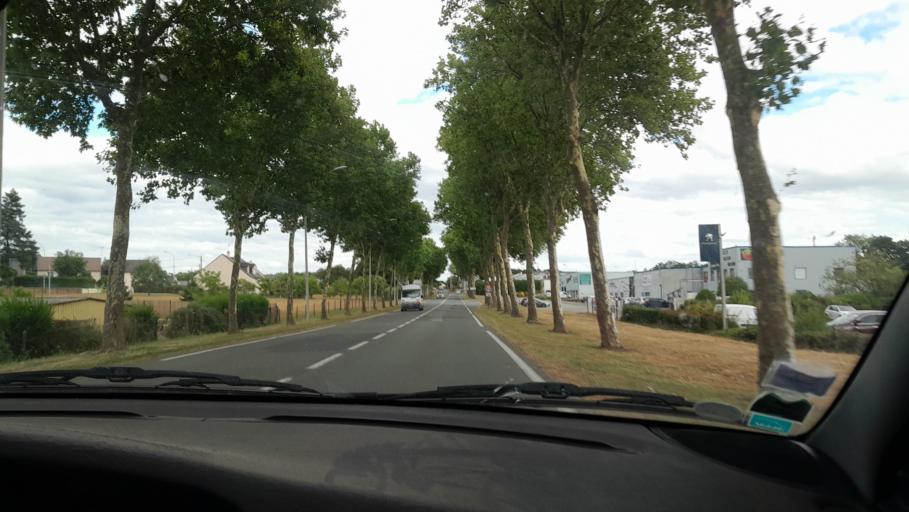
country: FR
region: Pays de la Loire
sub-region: Departement de la Mayenne
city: Craon
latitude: 47.8431
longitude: -0.9561
